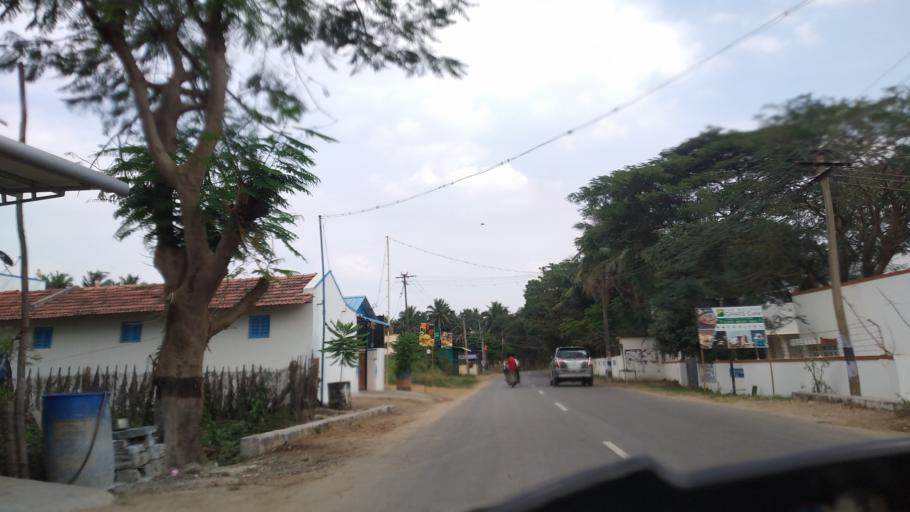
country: IN
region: Tamil Nadu
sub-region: Coimbatore
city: Perur
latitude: 10.9626
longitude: 76.7441
